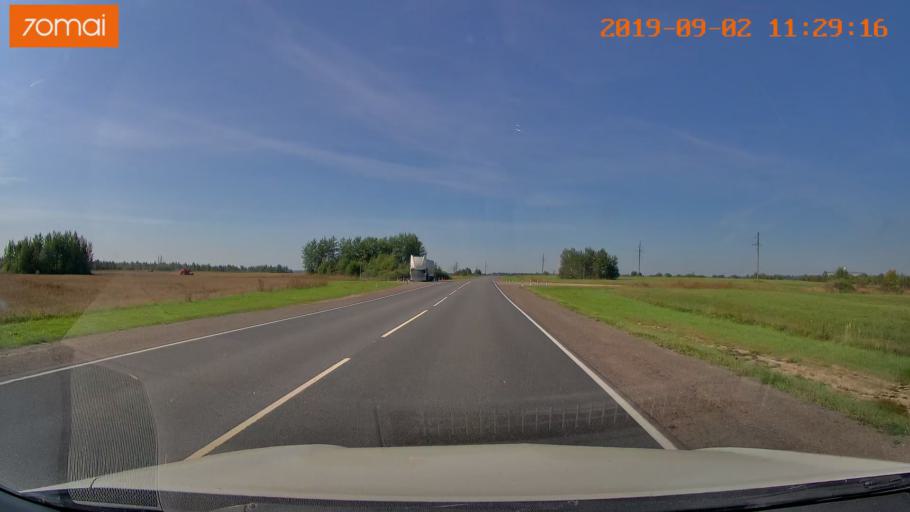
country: RU
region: Smolensk
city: Roslavl'
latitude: 53.9902
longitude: 32.8684
